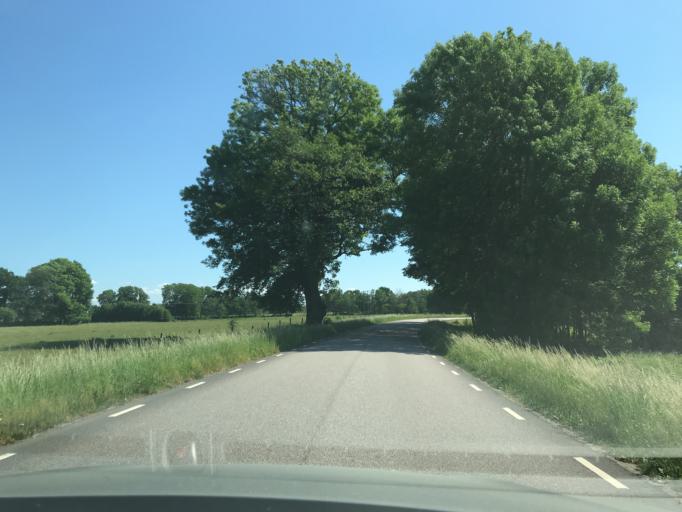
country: SE
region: Vaestra Goetaland
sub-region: Gotene Kommun
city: Kallby
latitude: 58.5325
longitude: 13.3234
